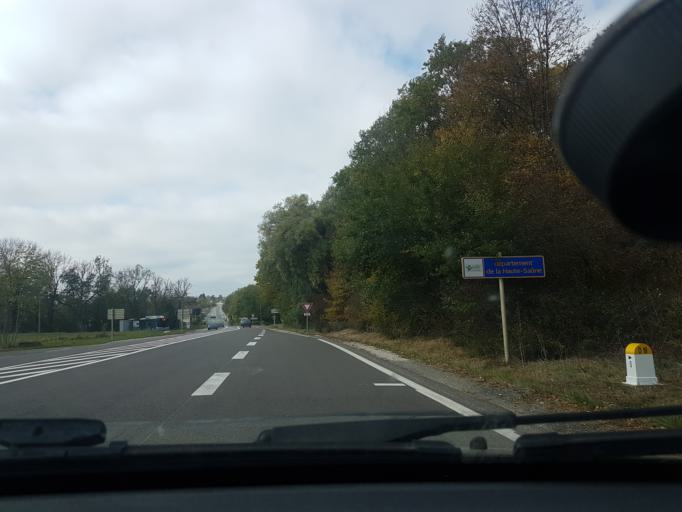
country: FR
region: Franche-Comte
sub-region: Departement de la Haute-Saone
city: Chalonvillars
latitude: 47.6410
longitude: 6.7976
